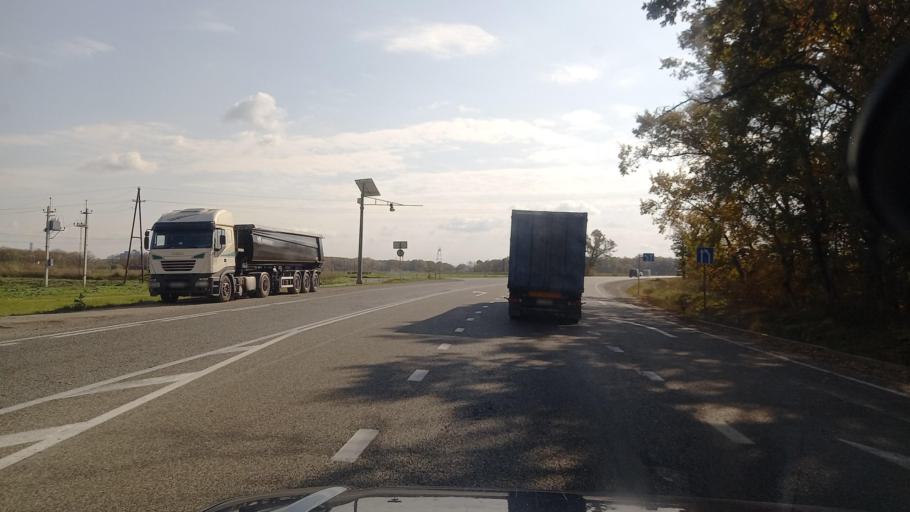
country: RU
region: Krasnodarskiy
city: Novoukrainskiy
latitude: 44.8842
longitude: 38.0890
